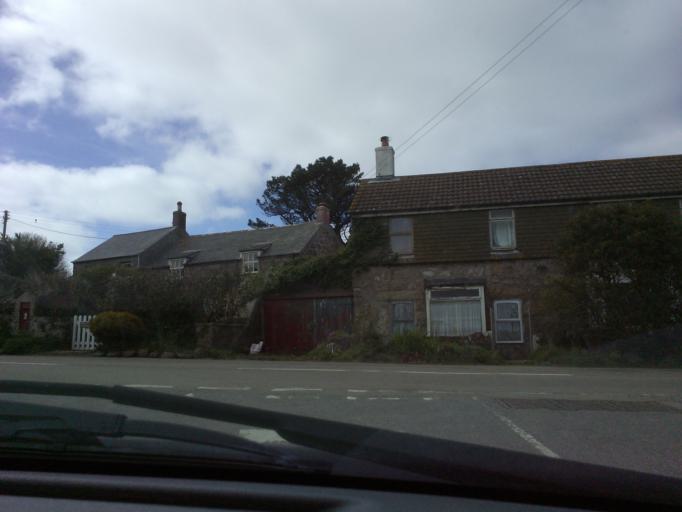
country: GB
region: England
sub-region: Cornwall
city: St. Buryan
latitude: 50.0599
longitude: -5.6361
